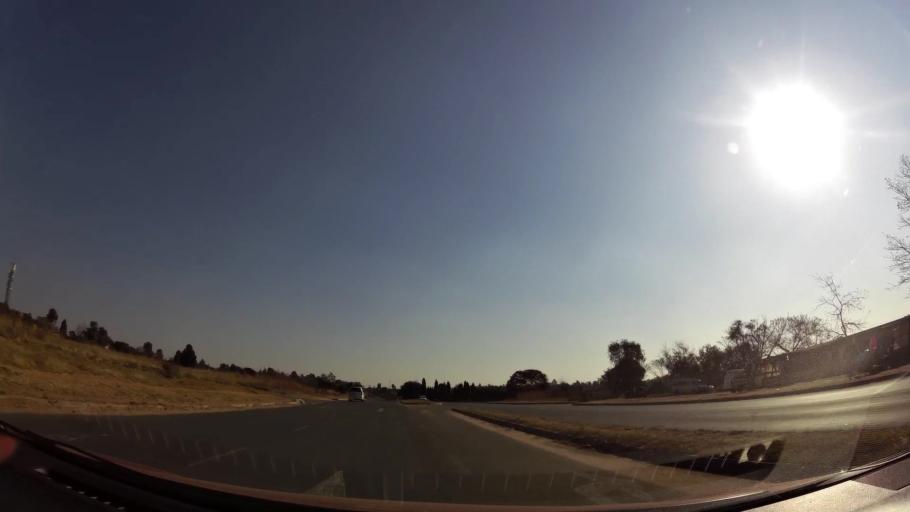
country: ZA
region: Gauteng
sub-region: West Rand District Municipality
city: Muldersdriseloop
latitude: -26.0428
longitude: 27.9111
